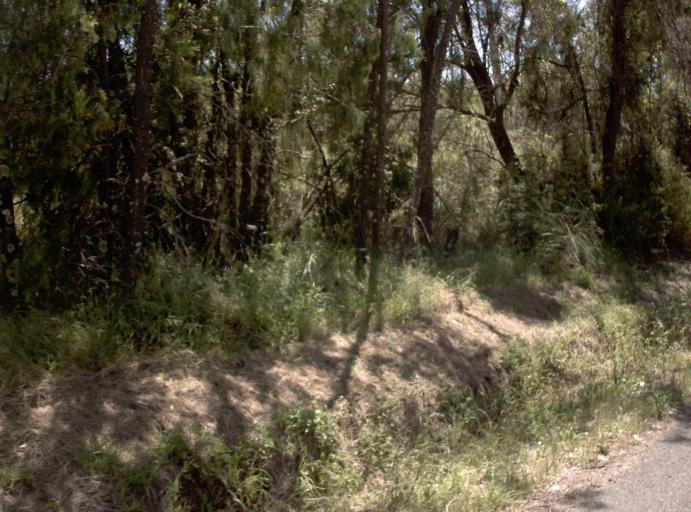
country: AU
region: Victoria
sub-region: East Gippsland
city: Lakes Entrance
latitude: -37.8303
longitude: 148.0315
